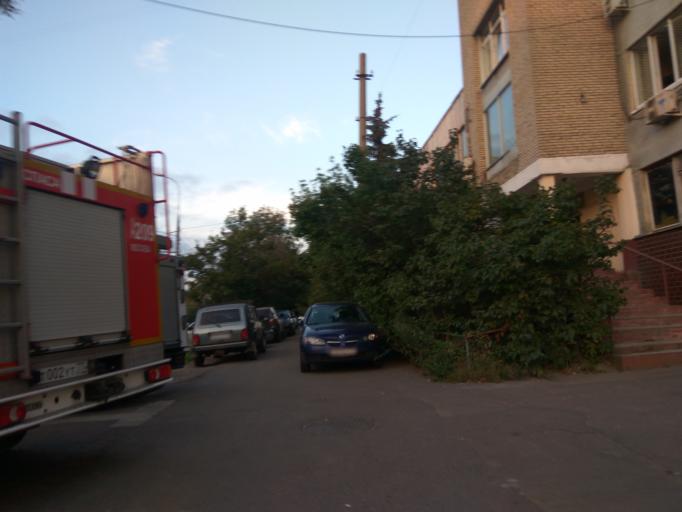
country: RU
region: Moscow
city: Mar'ino
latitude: 55.6578
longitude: 37.7310
